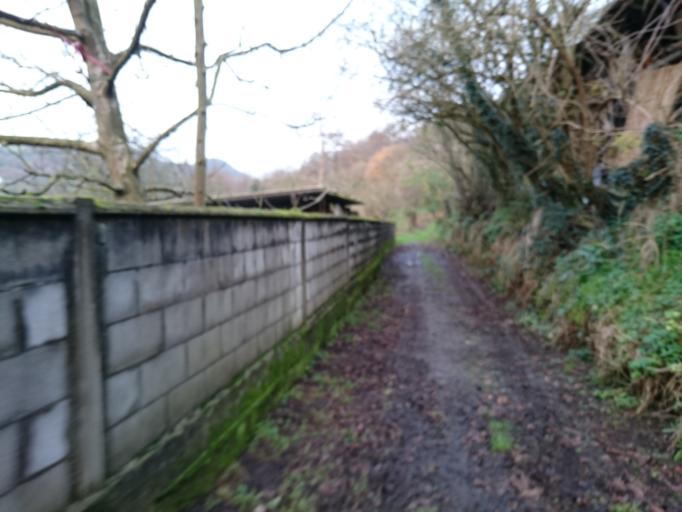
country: ES
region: Asturias
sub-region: Province of Asturias
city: Oviedo
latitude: 43.3197
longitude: -5.7990
